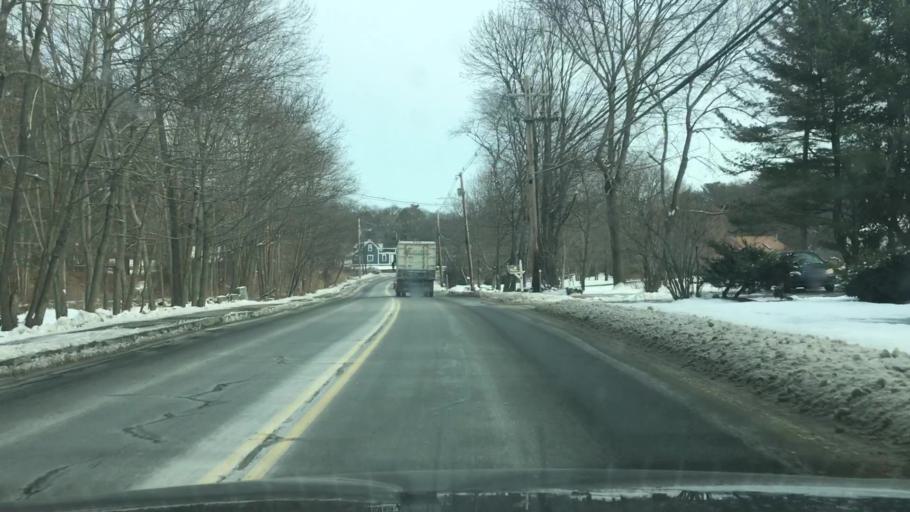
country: US
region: Massachusetts
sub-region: Essex County
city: Middleton
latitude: 42.5961
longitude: -71.0034
